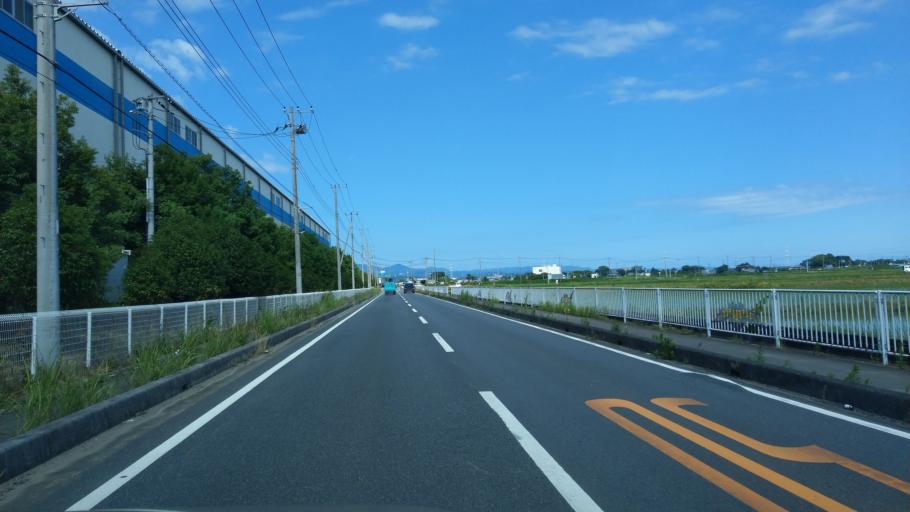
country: JP
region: Saitama
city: Sakado
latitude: 35.9885
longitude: 139.4627
